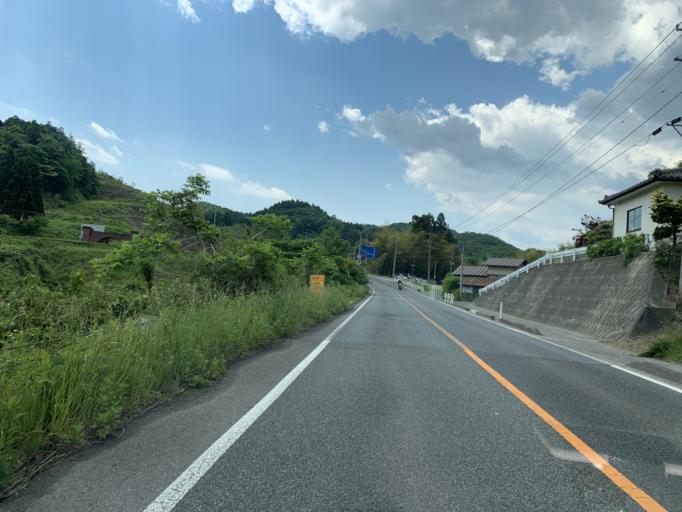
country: JP
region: Miyagi
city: Matsushima
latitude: 38.4215
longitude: 141.0591
